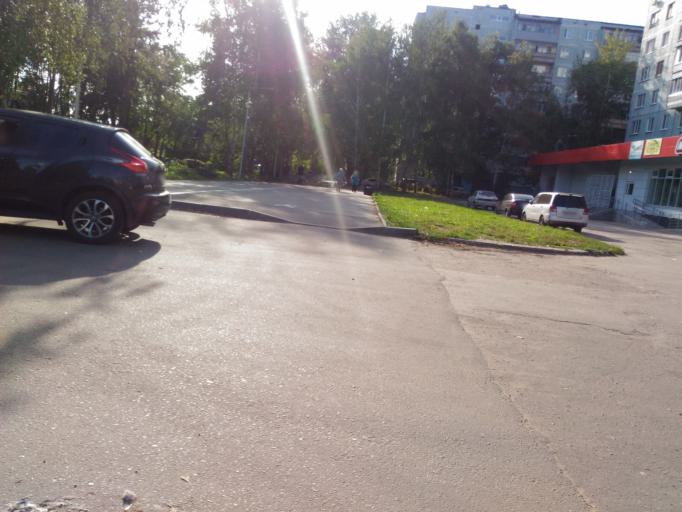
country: RU
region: Ulyanovsk
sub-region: Ulyanovskiy Rayon
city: Ulyanovsk
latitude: 54.3532
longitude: 48.5310
